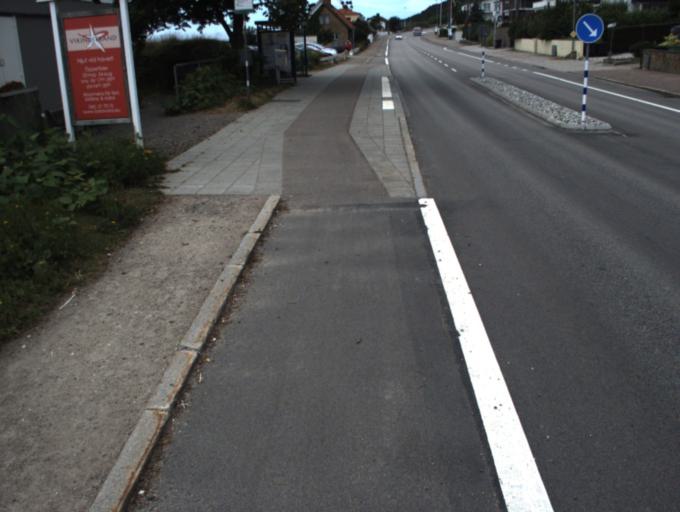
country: SE
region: Skane
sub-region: Helsingborg
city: Helsingborg
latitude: 56.0724
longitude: 12.6688
